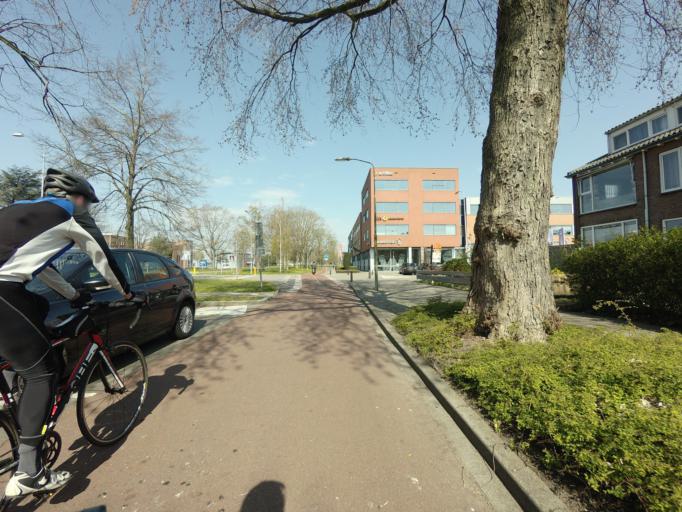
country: NL
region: Gelderland
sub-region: Gemeente Harderwijk
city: Harderwijk
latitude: 52.3375
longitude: 5.6334
